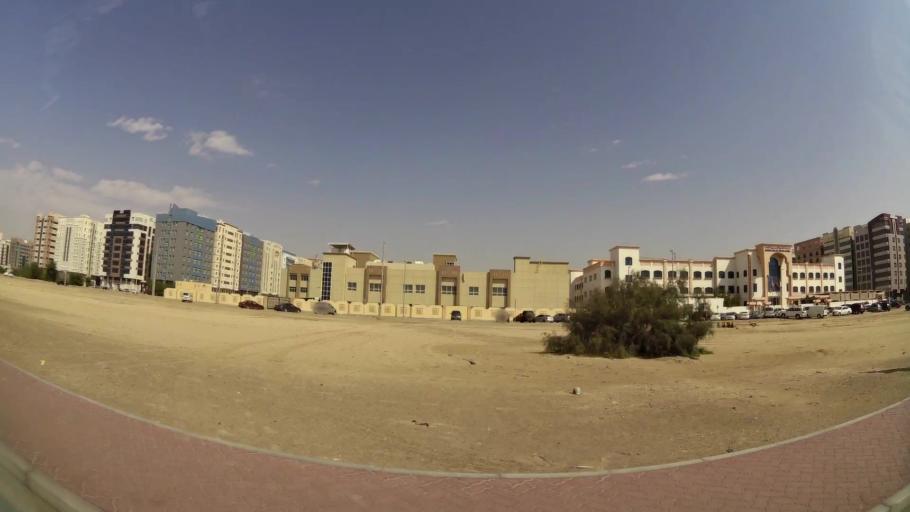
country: AE
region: Abu Dhabi
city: Abu Dhabi
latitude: 24.3391
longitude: 54.5294
